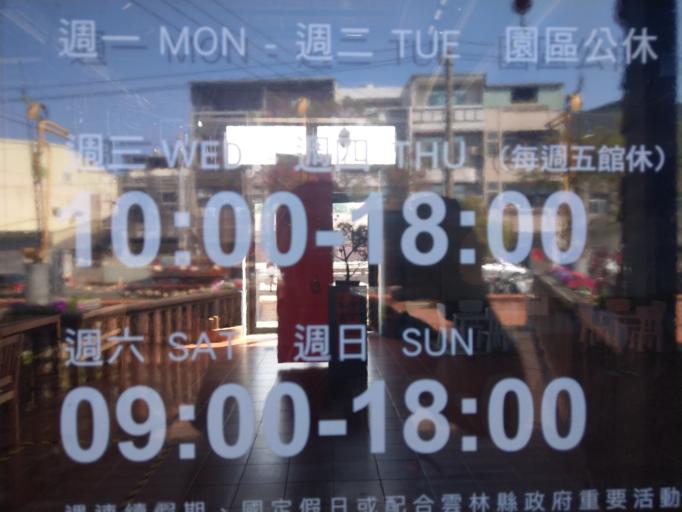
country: TW
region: Taiwan
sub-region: Yunlin
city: Douliu
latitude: 23.6742
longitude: 120.4817
